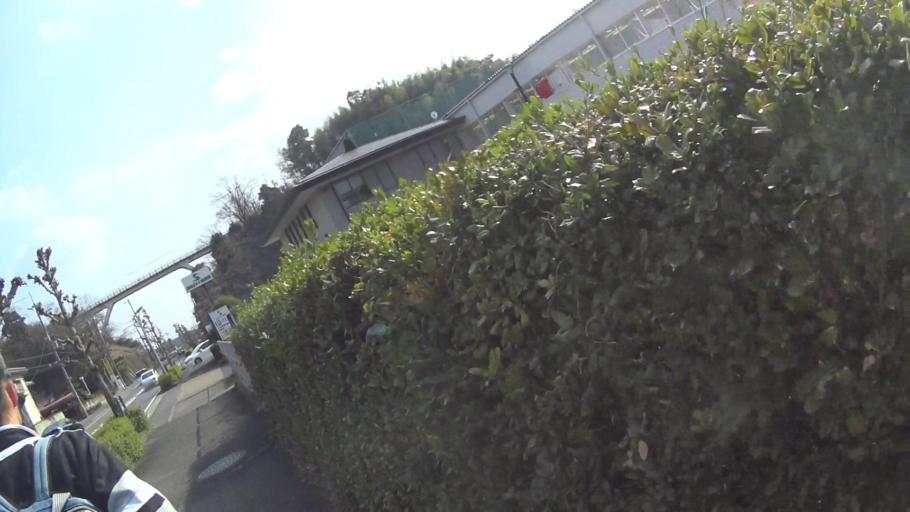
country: JP
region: Nara
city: Nara-shi
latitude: 34.7031
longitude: 135.8271
